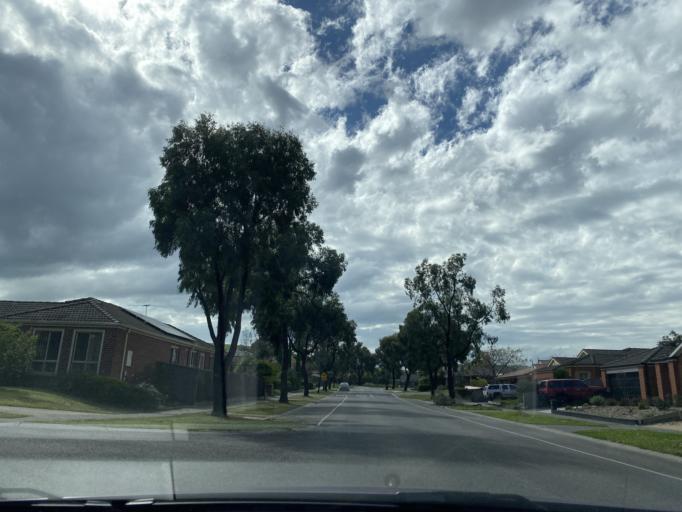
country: AU
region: Victoria
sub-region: Whittlesea
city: Mernda
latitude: -37.6259
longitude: 145.0932
